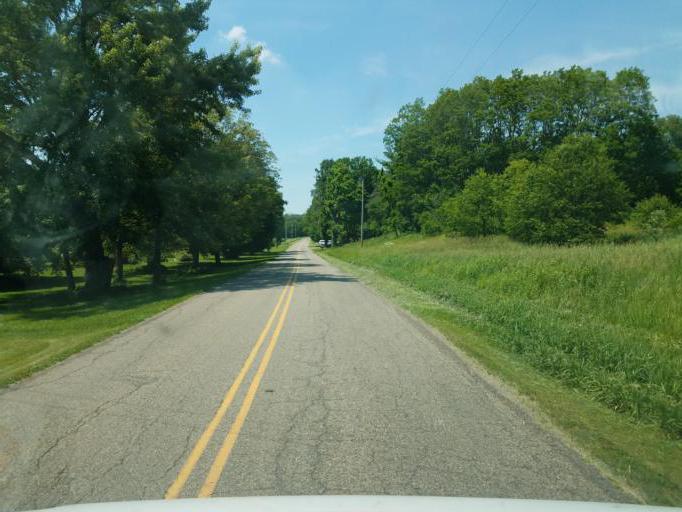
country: US
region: Ohio
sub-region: Knox County
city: Danville
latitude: 40.4934
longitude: -82.3538
